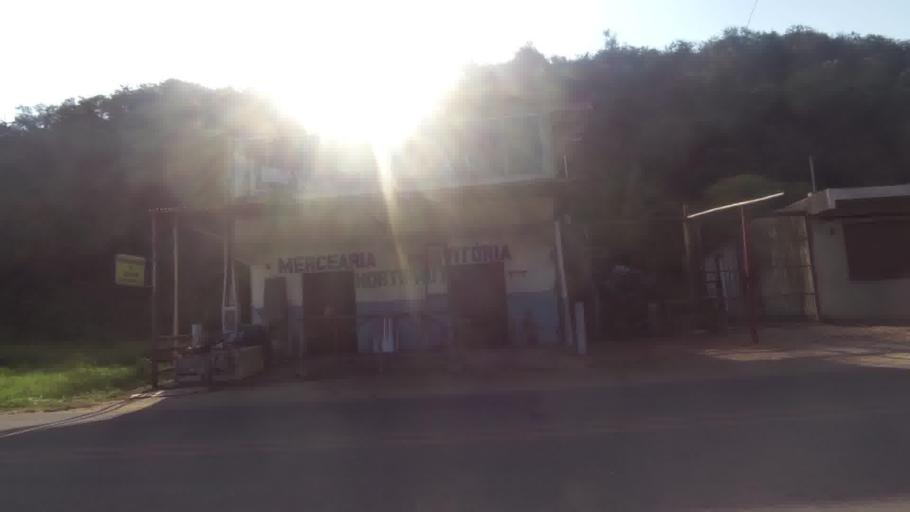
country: BR
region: Espirito Santo
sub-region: Piuma
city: Piuma
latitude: -20.8593
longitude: -40.7564
